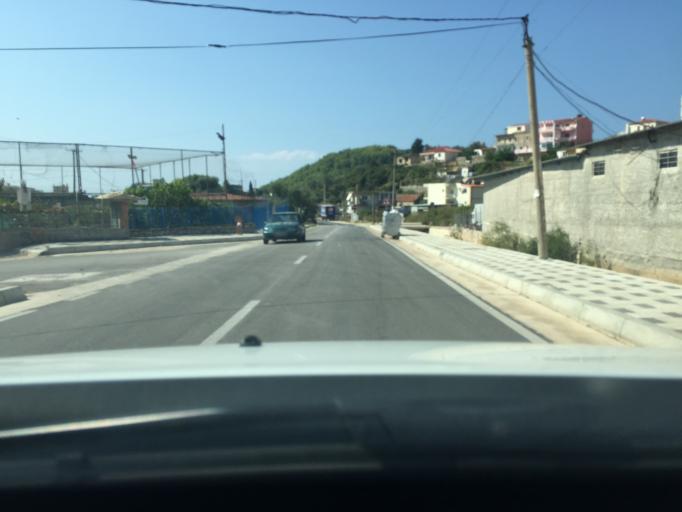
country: AL
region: Vlore
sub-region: Rrethi i Vlores
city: Himare
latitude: 40.1090
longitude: 19.7428
